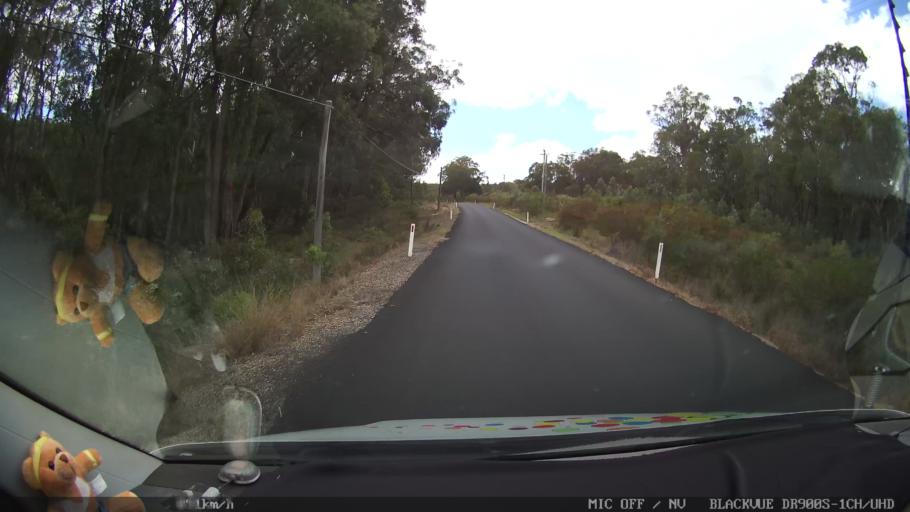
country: AU
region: New South Wales
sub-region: Glen Innes Severn
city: Glen Innes
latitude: -29.4386
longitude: 151.6262
